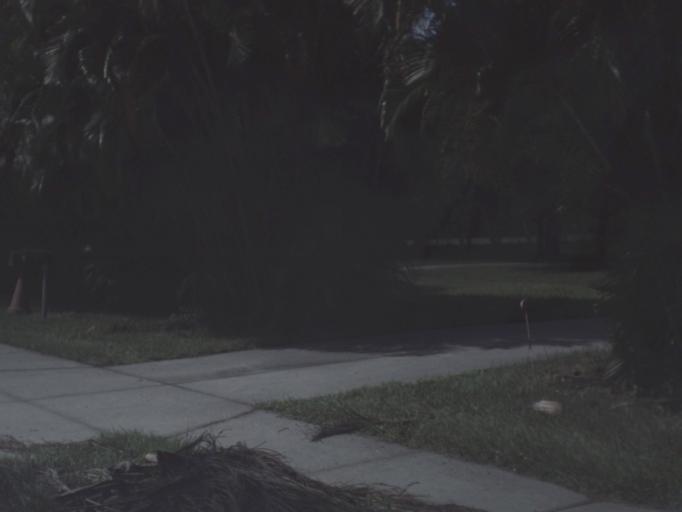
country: US
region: Florida
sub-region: Lee County
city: Whiskey Creek
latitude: 26.5742
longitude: -81.8998
